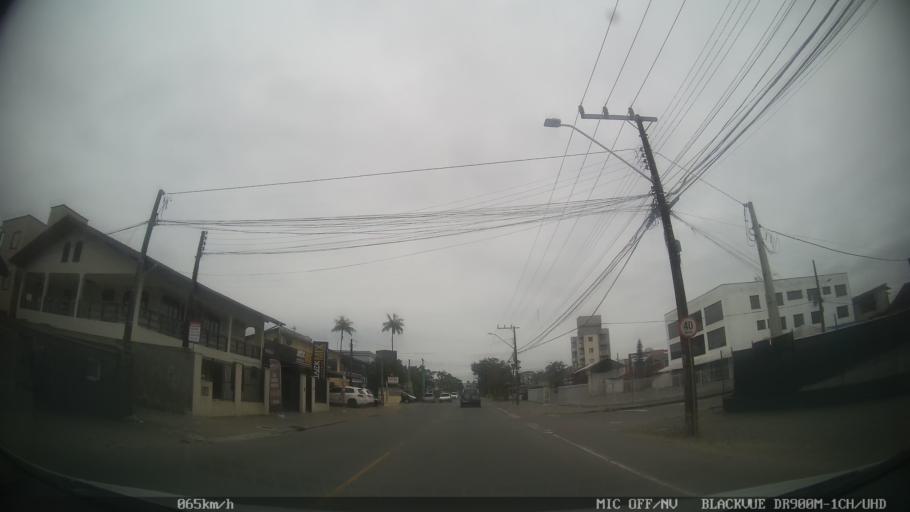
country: BR
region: Santa Catarina
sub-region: Joinville
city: Joinville
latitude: -26.3228
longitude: -48.8349
